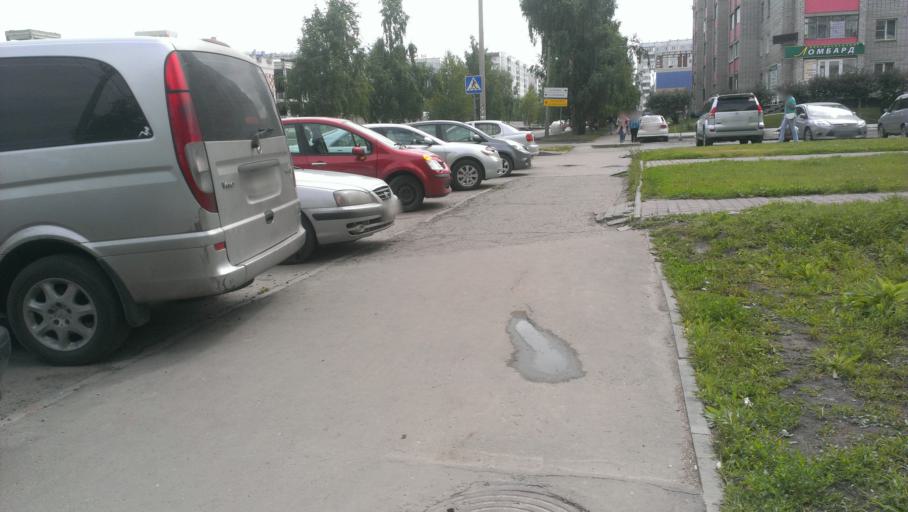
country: RU
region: Altai Krai
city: Novosilikatnyy
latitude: 53.3375
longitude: 83.6774
